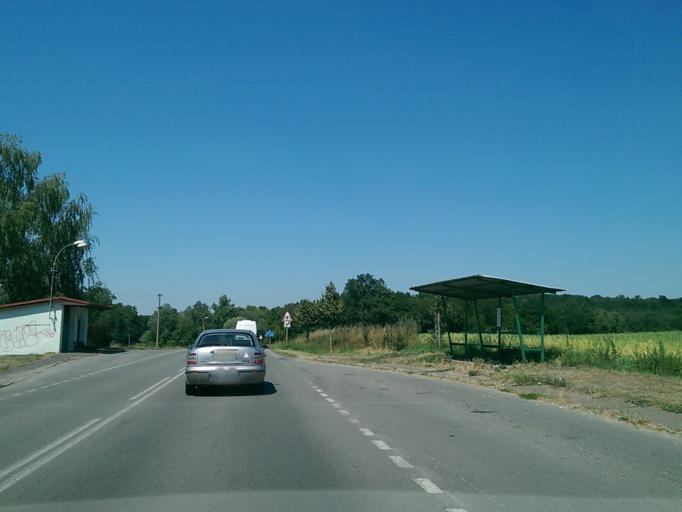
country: CZ
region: Central Bohemia
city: Benatky nad Jizerou
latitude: 50.3079
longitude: 14.8539
